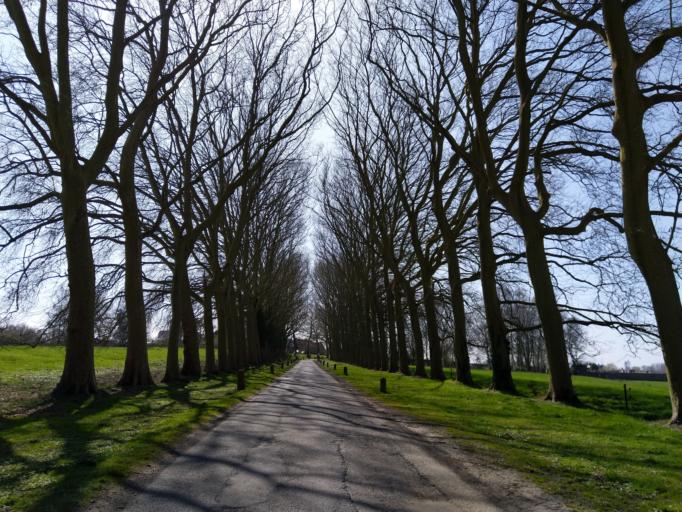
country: BE
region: Wallonia
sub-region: Province du Hainaut
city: Silly
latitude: 50.6163
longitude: 3.9528
